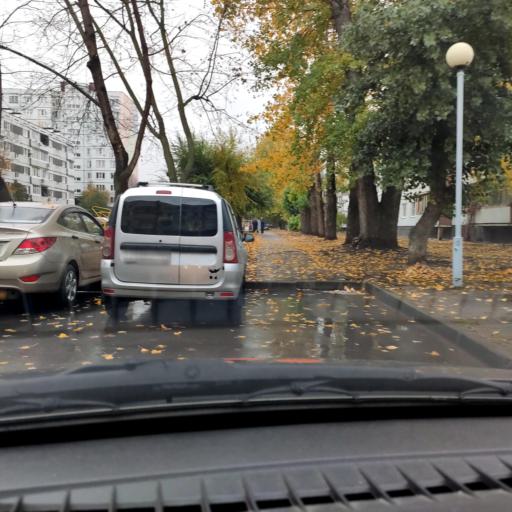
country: RU
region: Samara
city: Tol'yatti
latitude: 53.5212
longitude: 49.2878
